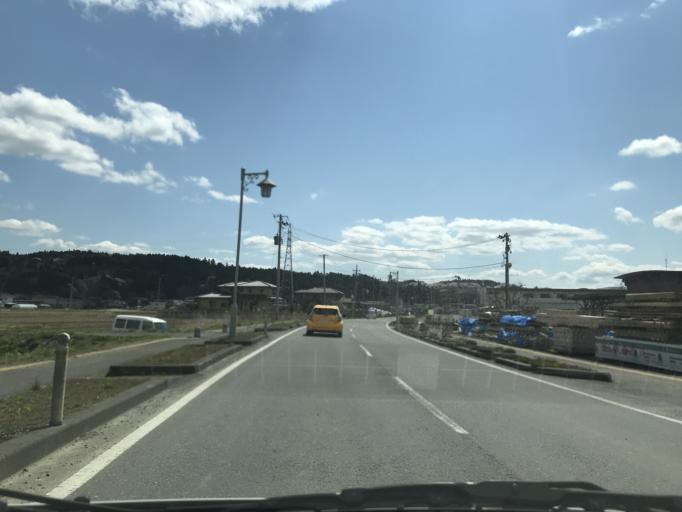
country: JP
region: Miyagi
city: Wakuya
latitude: 38.6552
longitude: 141.2732
